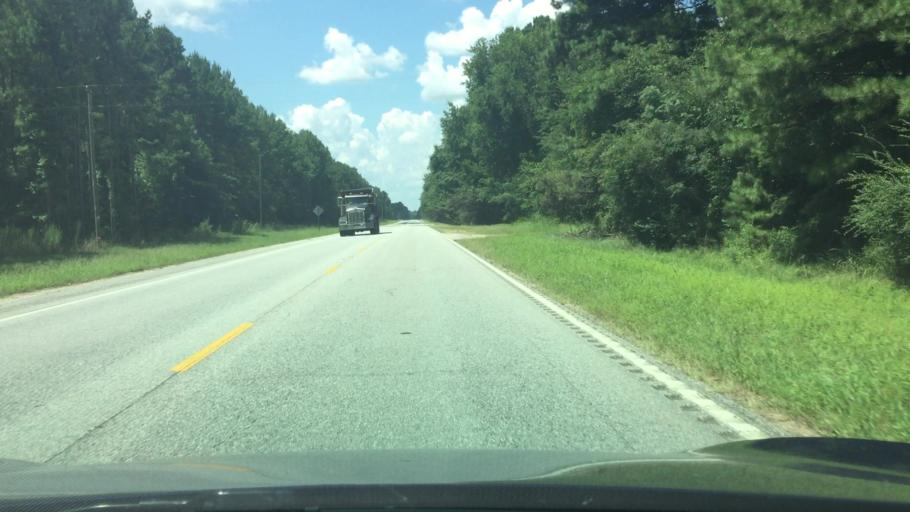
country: US
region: Alabama
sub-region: Montgomery County
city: Pike Road
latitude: 32.3889
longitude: -85.9811
